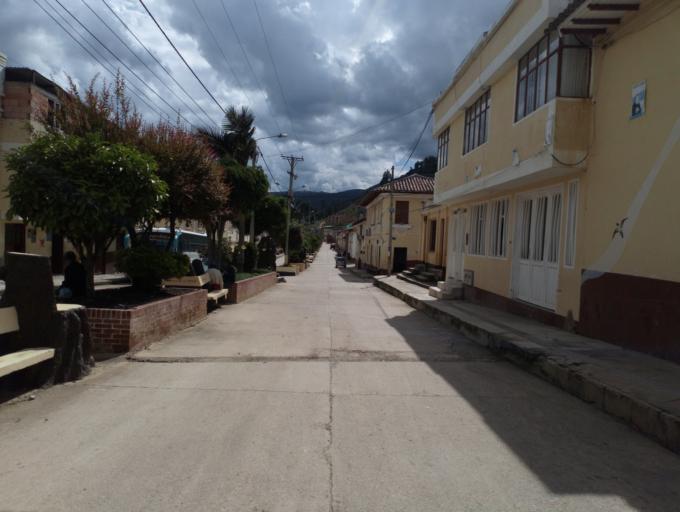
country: CO
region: Boyaca
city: Susacon
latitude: 6.1317
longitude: -72.7079
